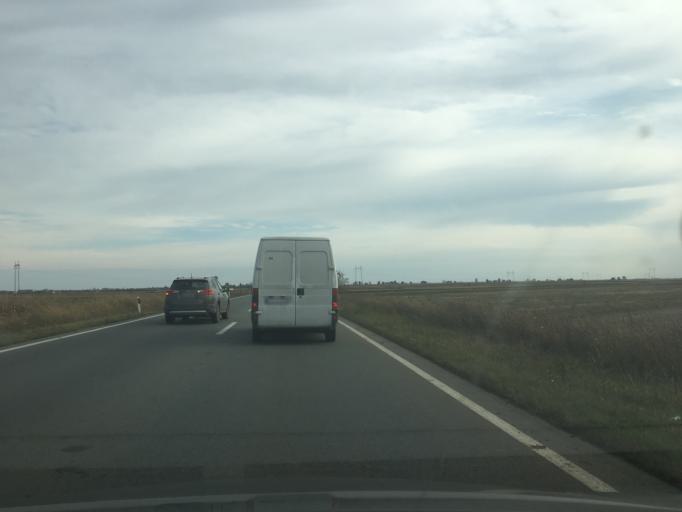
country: RS
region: Autonomna Pokrajina Vojvodina
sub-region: Juznobacki Okrug
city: Zabalj
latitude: 45.3492
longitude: 20.0417
